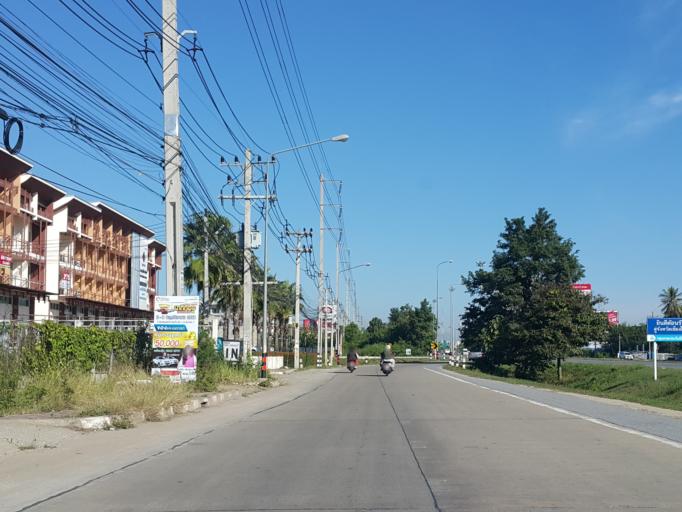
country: TH
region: Chiang Mai
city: Saraphi
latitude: 18.7537
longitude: 99.0316
